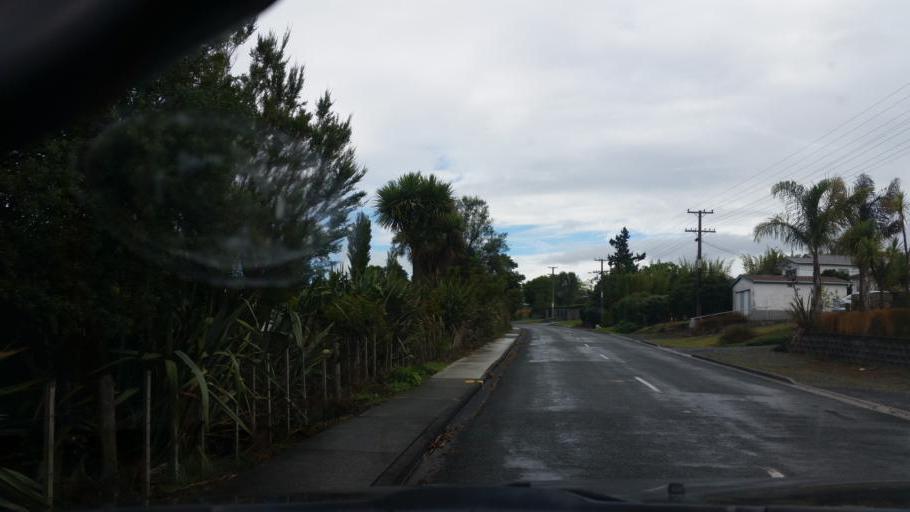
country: NZ
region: Northland
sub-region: Whangarei
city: Ruakaka
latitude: -36.1091
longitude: 174.3622
